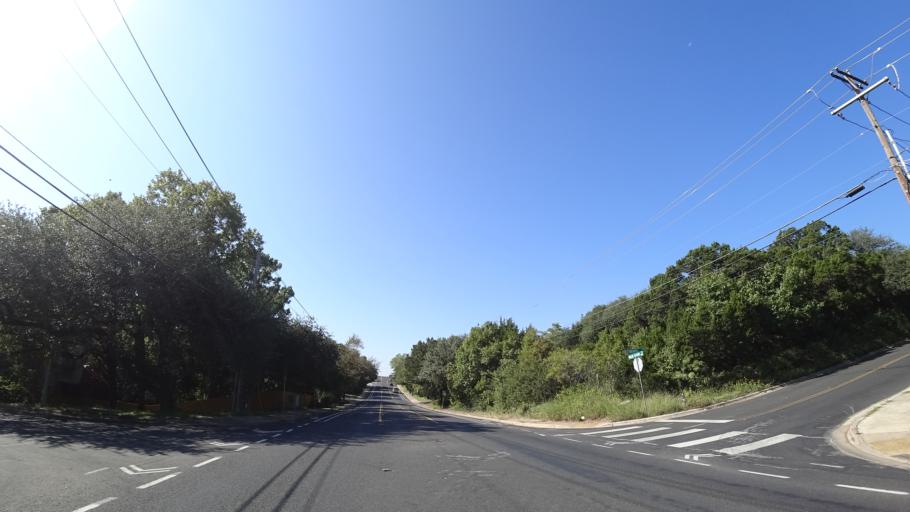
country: US
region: Texas
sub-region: Travis County
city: Rollingwood
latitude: 30.2643
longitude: -97.8076
